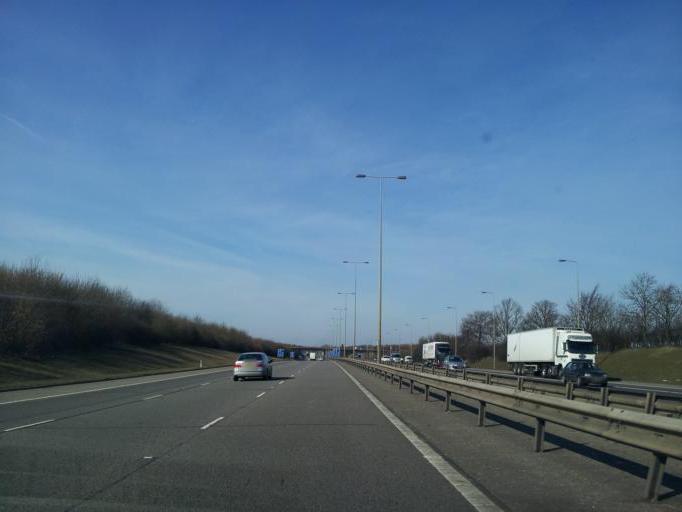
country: GB
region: England
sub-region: Cambridgeshire
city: Stilton
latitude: 52.5282
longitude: -0.3128
